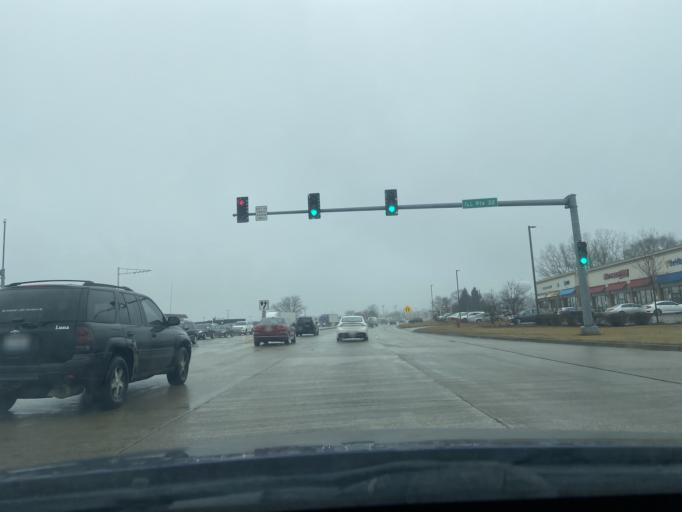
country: US
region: Illinois
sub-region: Lake County
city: Knollwood
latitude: 42.1903
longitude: -88.1069
